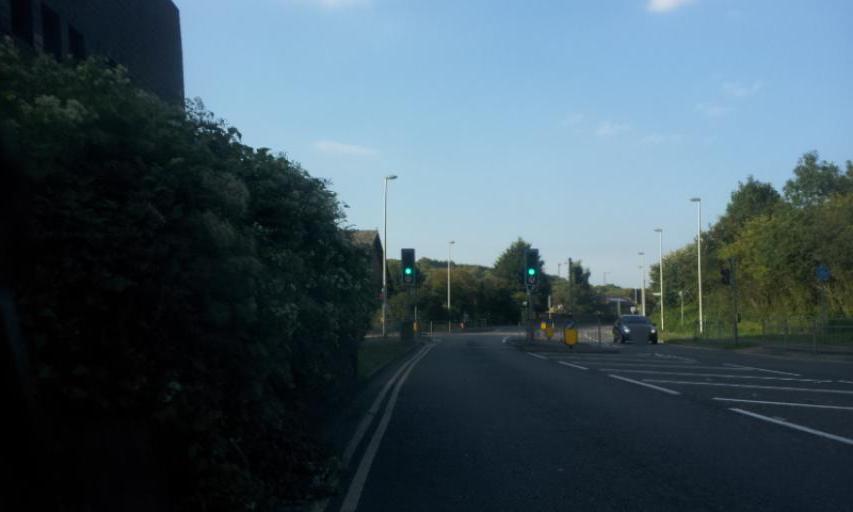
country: GB
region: England
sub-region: Kent
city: Chatham
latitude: 51.3539
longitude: 0.5355
